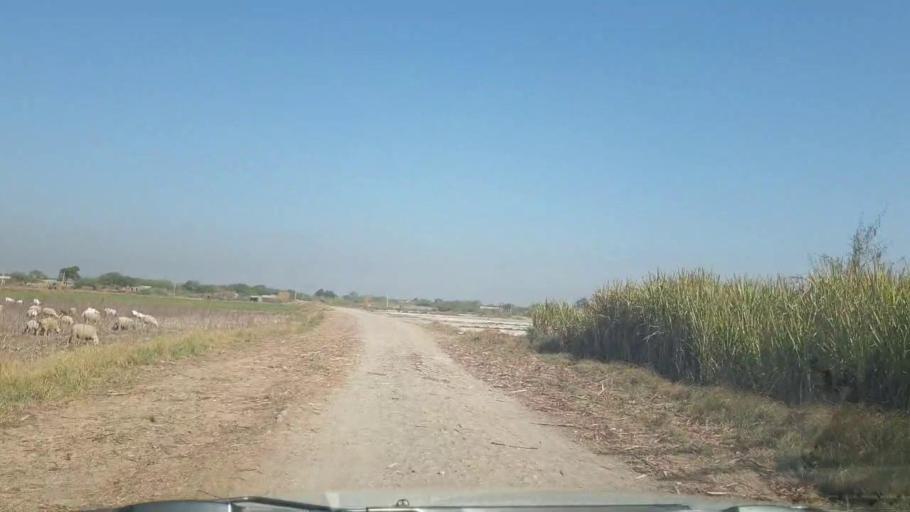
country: PK
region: Sindh
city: Mirpur Khas
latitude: 25.5129
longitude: 69.1495
